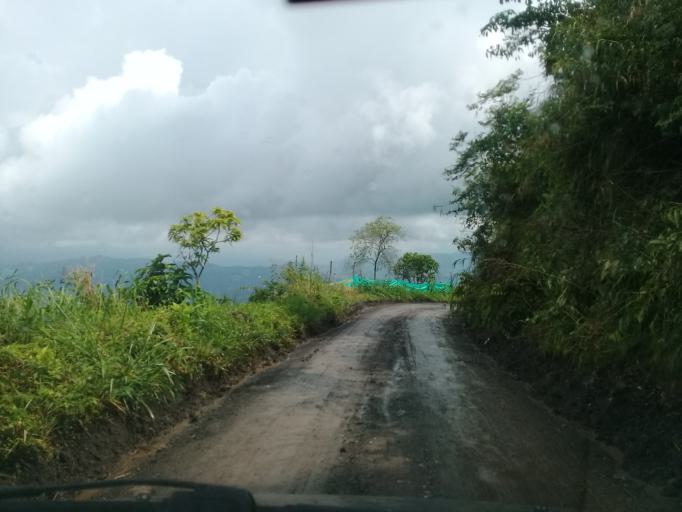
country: CO
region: Cundinamarca
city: Quipile
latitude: 4.7045
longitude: -74.5302
